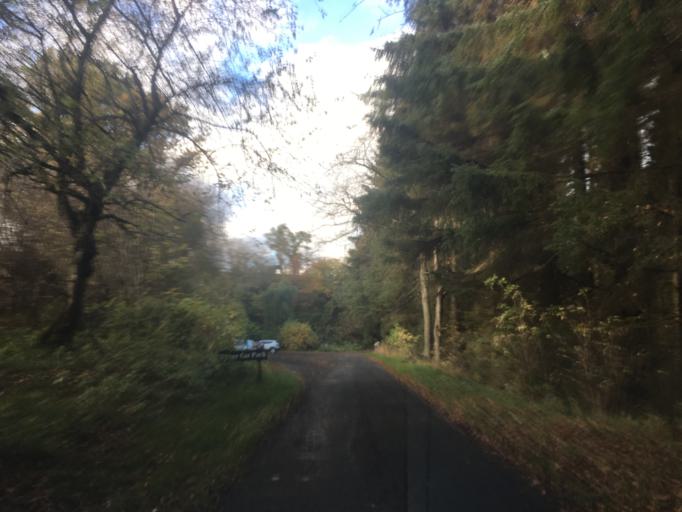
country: GB
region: Scotland
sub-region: East Lothian
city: Pencaitland
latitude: 55.8619
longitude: -2.8645
